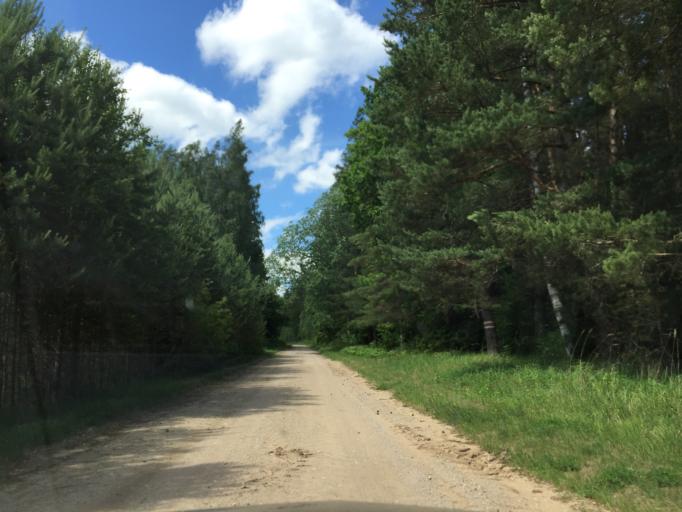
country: LV
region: Engure
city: Smarde
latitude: 56.9863
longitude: 23.2873
